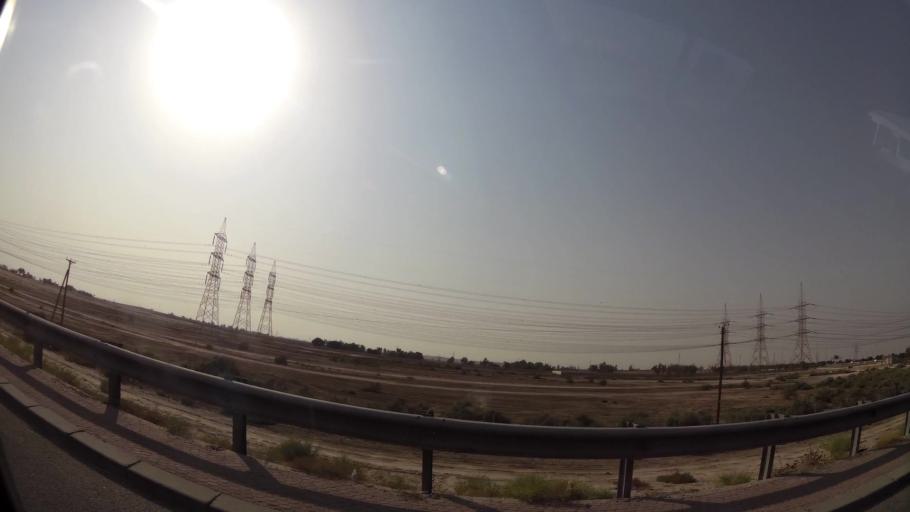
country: KW
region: Muhafazat al Jahra'
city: Al Jahra'
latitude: 29.3076
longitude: 47.7839
